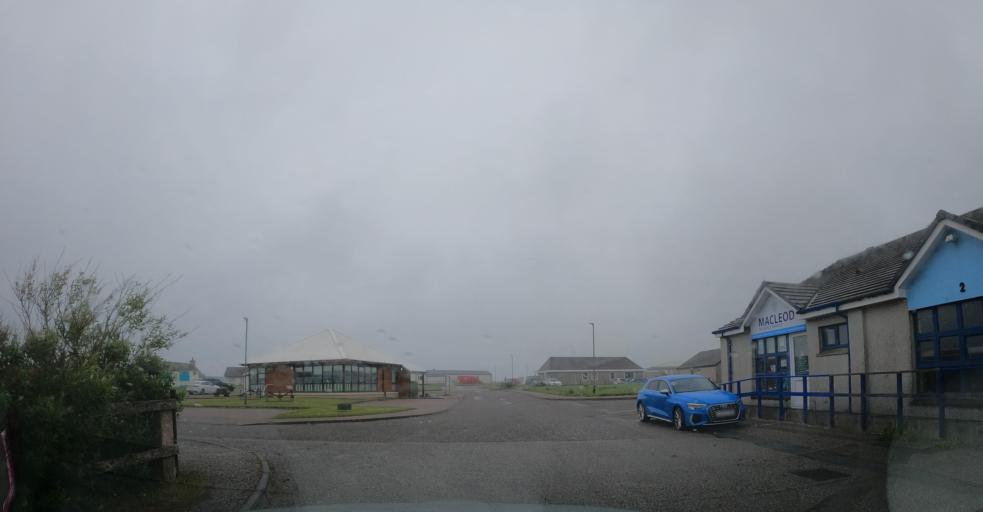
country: GB
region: Scotland
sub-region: Eilean Siar
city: Benbecula
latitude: 57.4725
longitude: -7.3785
